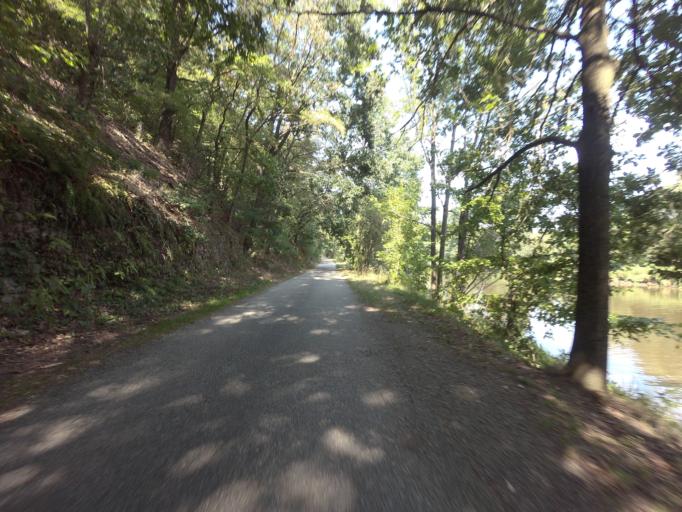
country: CZ
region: Jihocesky
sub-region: Okres Ceske Budejovice
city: Hluboka nad Vltavou
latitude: 49.0589
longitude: 14.4423
